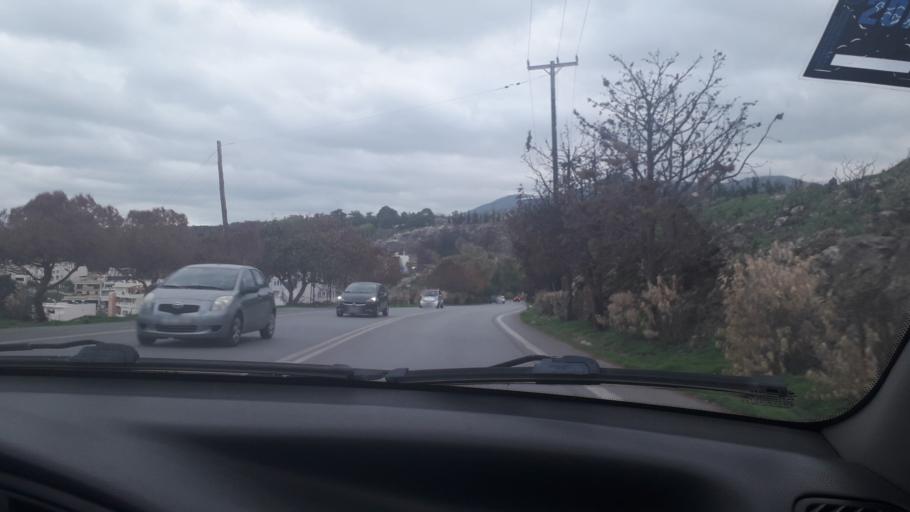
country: GR
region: Crete
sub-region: Nomos Rethymnis
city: Rethymno
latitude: 35.3585
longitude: 24.4698
